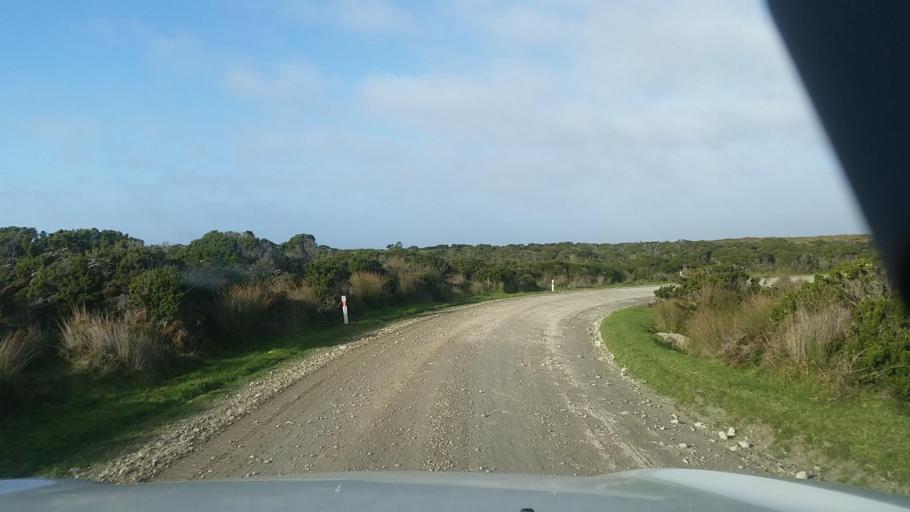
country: NZ
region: Chatham Islands
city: Waitangi
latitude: -43.7481
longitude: -176.3296
